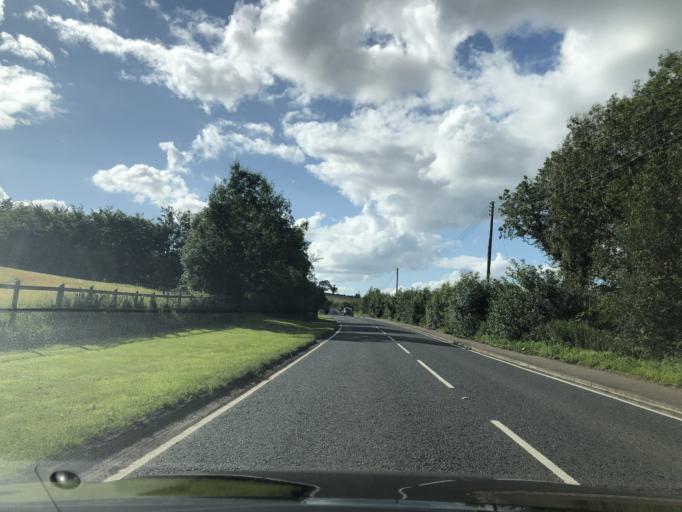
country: GB
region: Northern Ireland
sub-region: Castlereagh District
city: Dundonald
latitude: 54.5779
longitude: -5.7876
